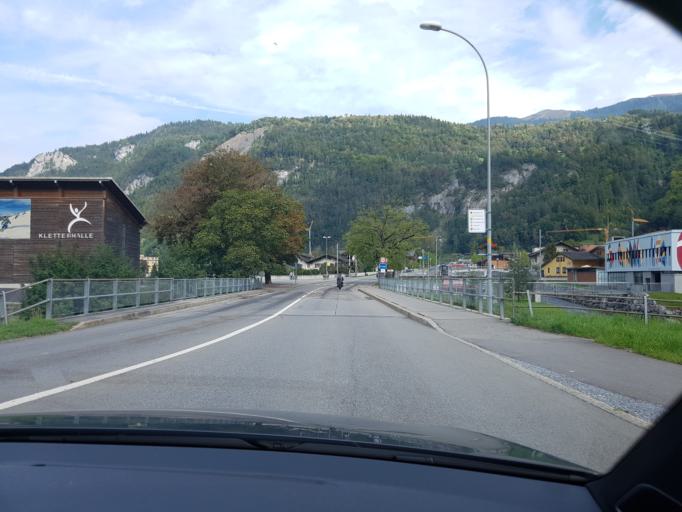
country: CH
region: Bern
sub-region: Interlaken-Oberhasli District
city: Meiringen
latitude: 46.7219
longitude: 8.1895
